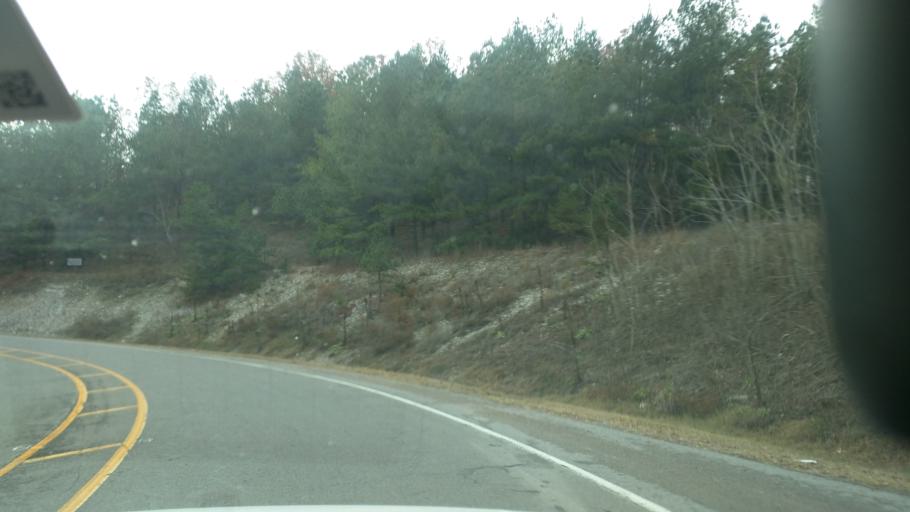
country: US
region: Oklahoma
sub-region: Cherokee County
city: Tahlequah
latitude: 35.9292
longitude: -94.8446
